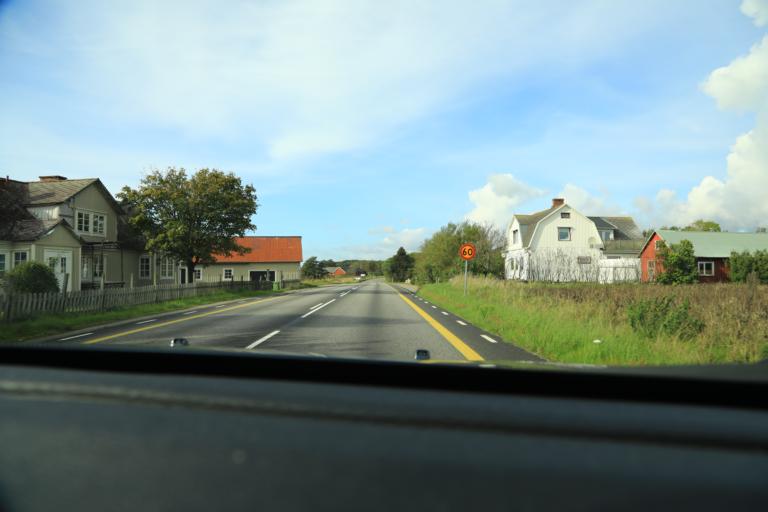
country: SE
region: Halland
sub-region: Varbergs Kommun
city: Traslovslage
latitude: 57.0355
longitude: 12.3268
